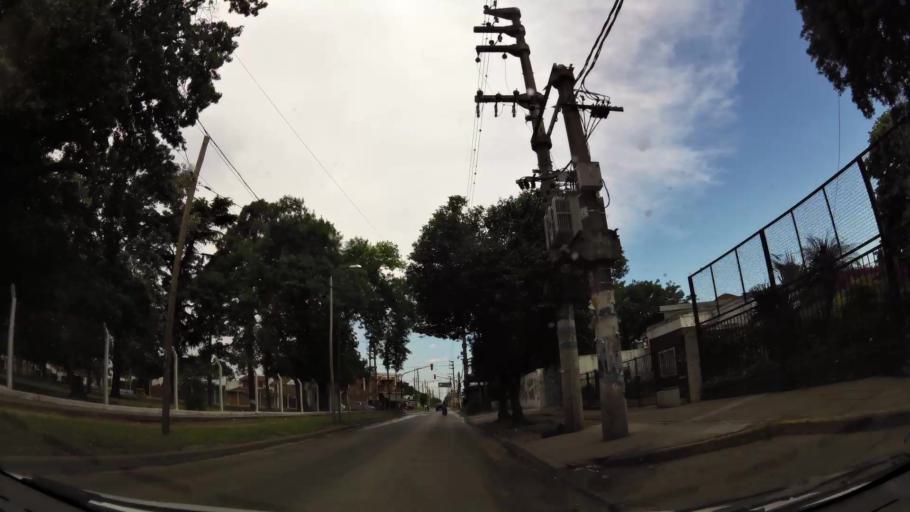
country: AR
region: Buenos Aires
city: Ituzaingo
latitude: -34.6365
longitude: -58.6938
